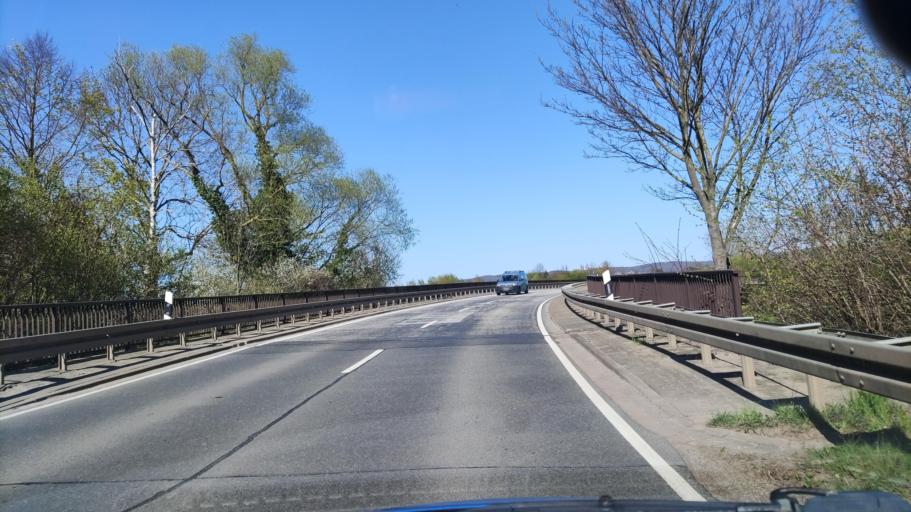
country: DE
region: Lower Saxony
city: Gronau
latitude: 52.0869
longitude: 9.7691
